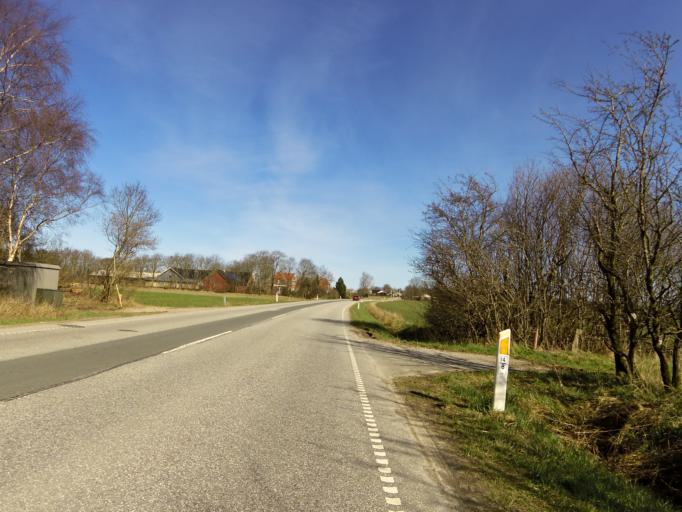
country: DK
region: South Denmark
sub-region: Vejen Kommune
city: Rodding
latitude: 55.3511
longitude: 8.9621
